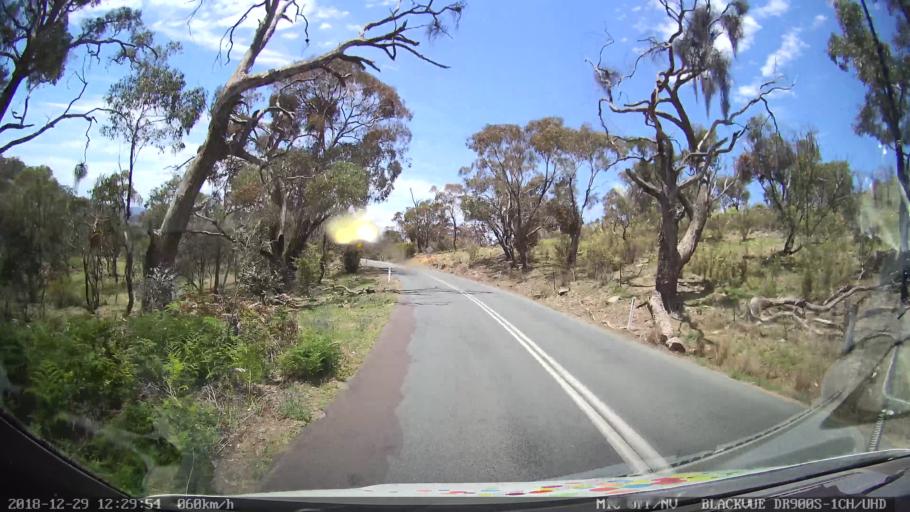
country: AU
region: Australian Capital Territory
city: Macarthur
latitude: -35.5017
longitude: 149.2318
